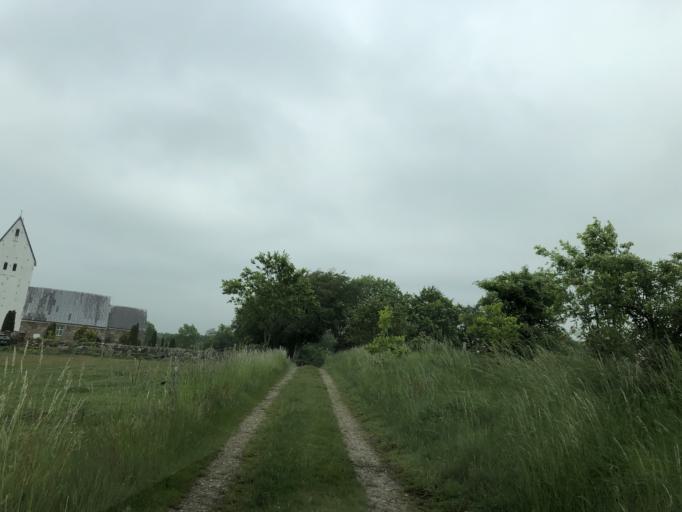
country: DK
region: Central Jutland
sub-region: Holstebro Kommune
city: Holstebro
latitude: 56.3352
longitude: 8.4814
